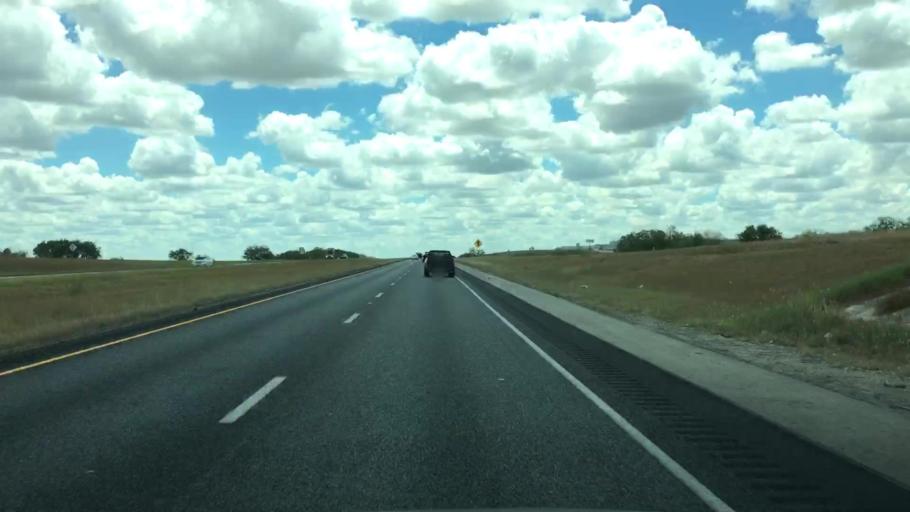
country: US
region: Texas
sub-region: Atascosa County
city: Pleasanton
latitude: 29.1058
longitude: -98.4326
